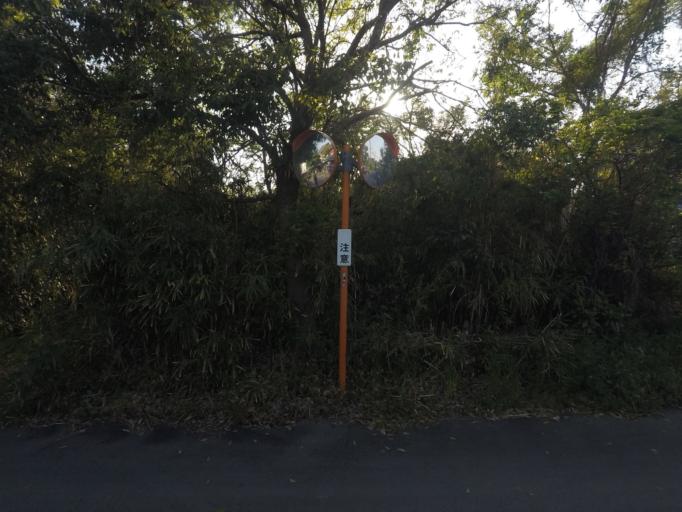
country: JP
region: Ibaraki
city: Ami
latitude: 36.0687
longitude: 140.2545
